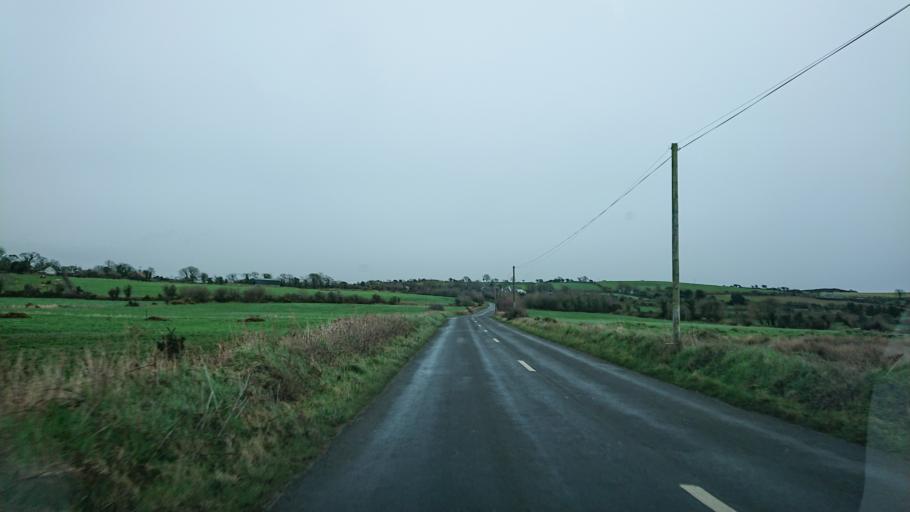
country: IE
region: Munster
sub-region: Waterford
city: Dunmore East
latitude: 52.2350
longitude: -7.0186
